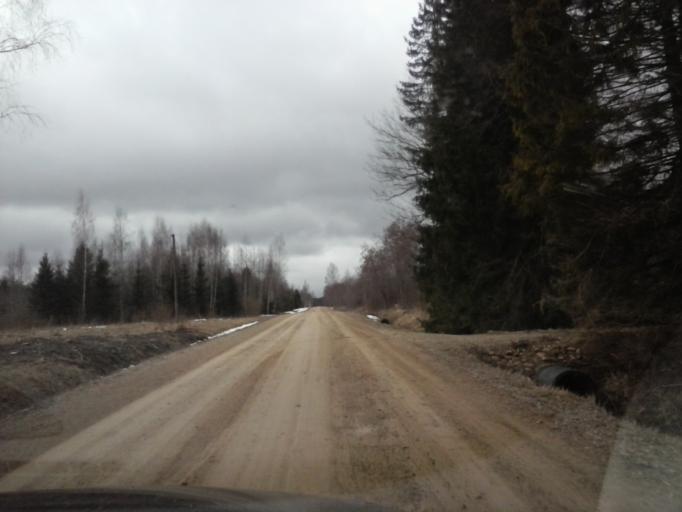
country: EE
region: Jogevamaa
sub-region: Mustvee linn
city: Mustvee
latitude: 59.0835
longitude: 26.8640
